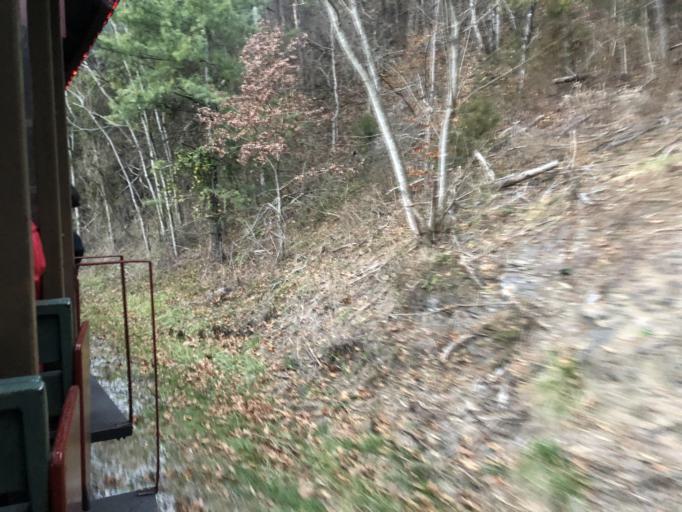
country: US
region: Tennessee
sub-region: Sevier County
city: Pigeon Forge
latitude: 35.7966
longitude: -83.5254
